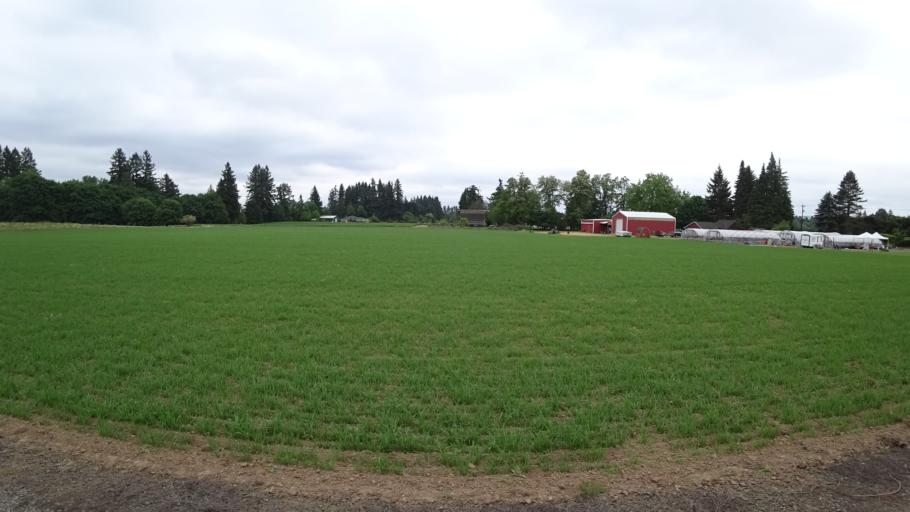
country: US
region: Oregon
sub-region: Washington County
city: Hillsboro
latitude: 45.4946
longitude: -122.9897
